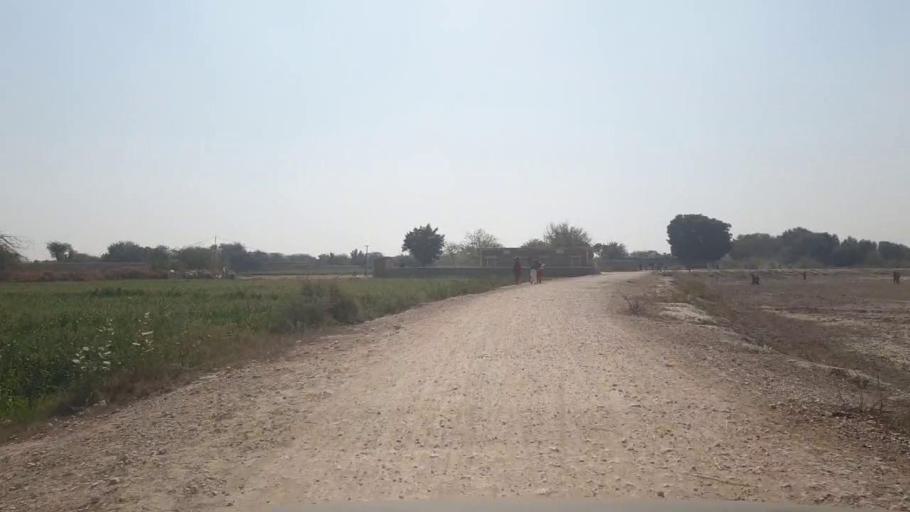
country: PK
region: Sindh
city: Chambar
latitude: 25.2341
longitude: 68.8233
